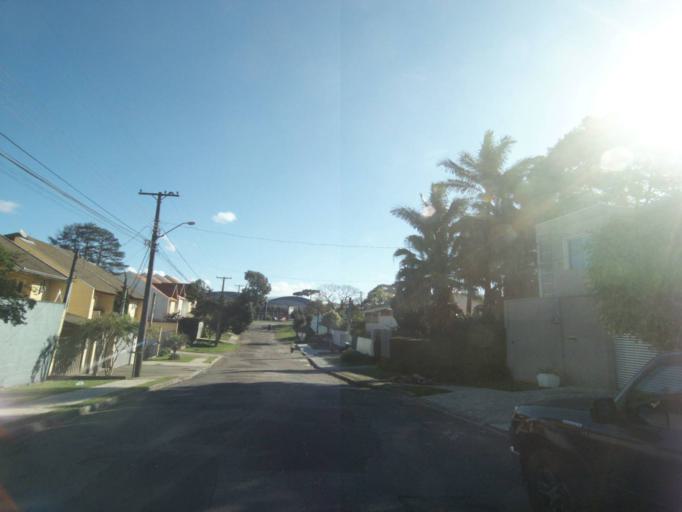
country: BR
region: Parana
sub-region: Curitiba
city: Curitiba
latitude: -25.3918
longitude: -49.2567
